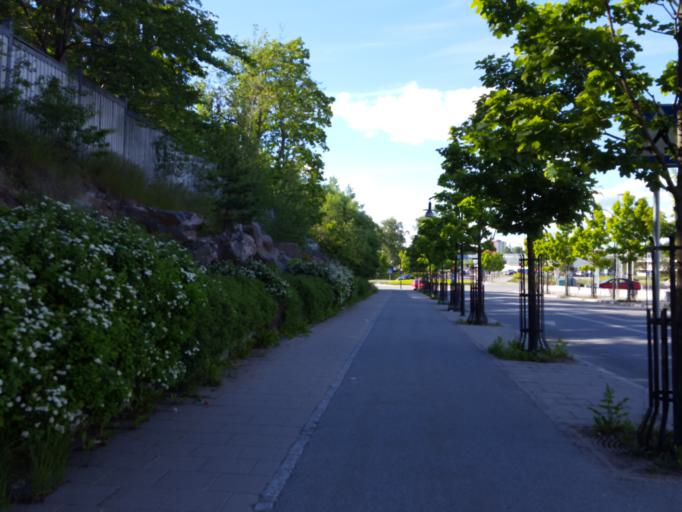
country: SE
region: Stockholm
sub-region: Sollentuna Kommun
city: Sollentuna
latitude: 59.4367
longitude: 17.9355
